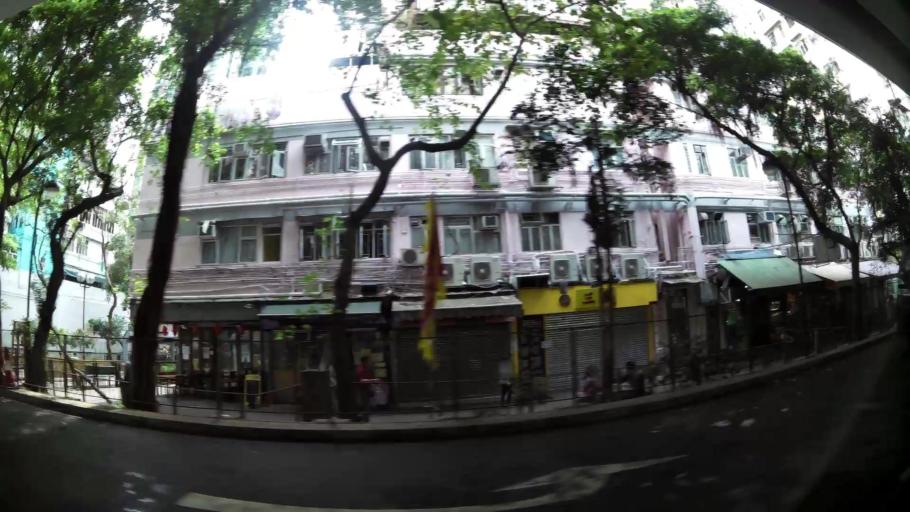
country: HK
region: Wanchai
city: Wan Chai
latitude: 22.2802
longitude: 114.2303
